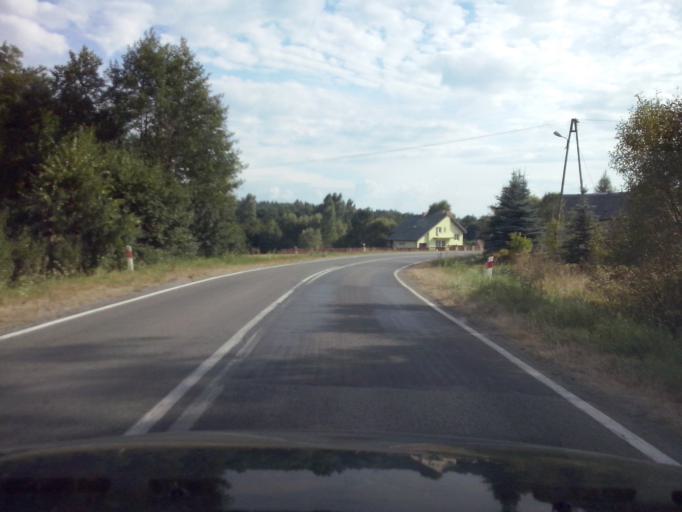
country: PL
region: Swietokrzyskie
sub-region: Powiat kielecki
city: Rakow
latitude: 50.7066
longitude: 21.0579
